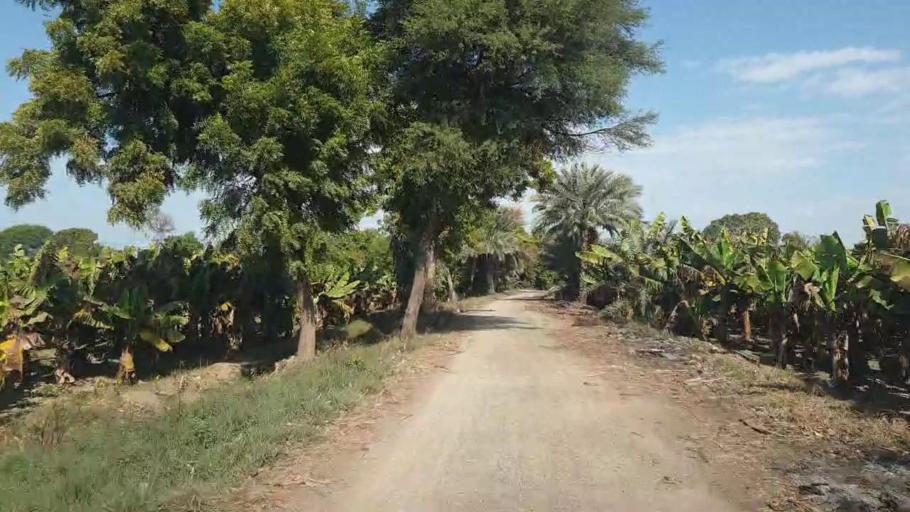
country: PK
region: Sindh
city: Hala
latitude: 25.9756
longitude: 68.3612
